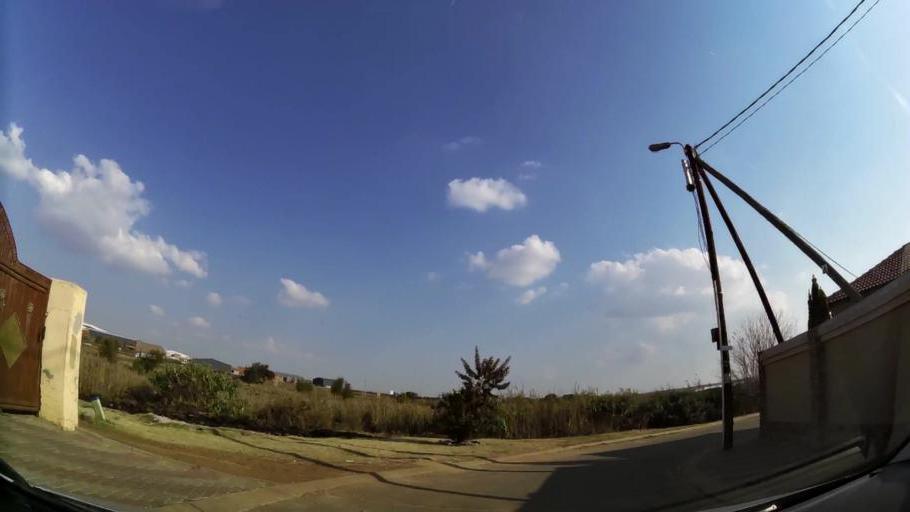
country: ZA
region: Gauteng
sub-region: Ekurhuleni Metropolitan Municipality
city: Tembisa
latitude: -25.9570
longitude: 28.2162
